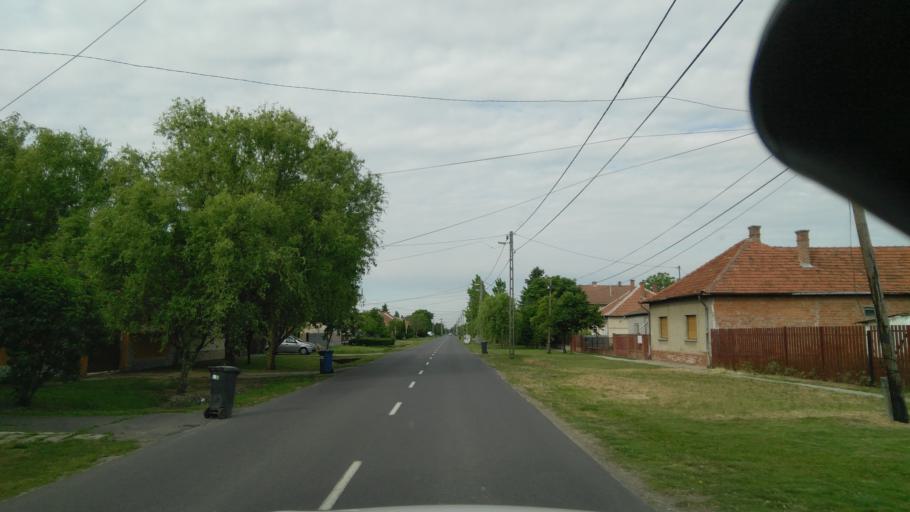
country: HU
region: Bekes
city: Ketegyhaza
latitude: 46.5485
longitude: 21.1819
